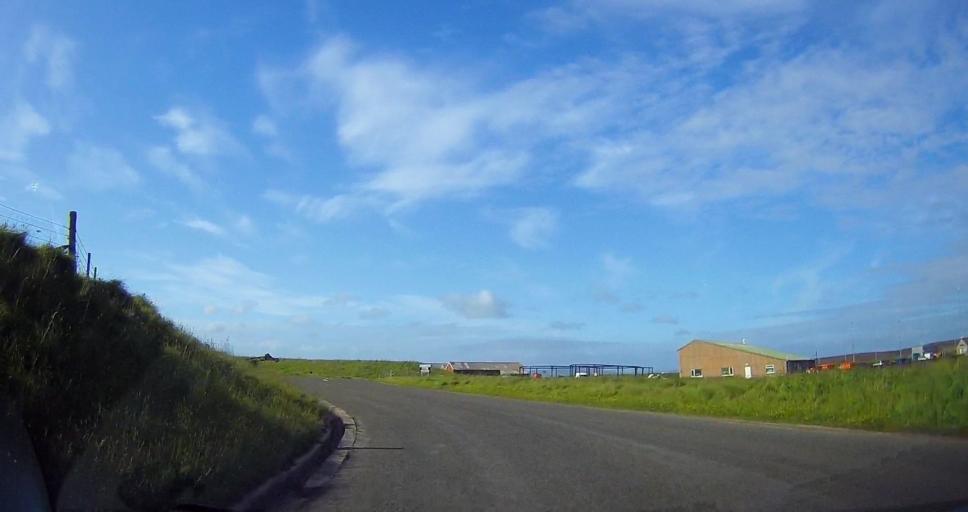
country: GB
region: Scotland
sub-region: Orkney Islands
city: Stromness
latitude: 58.8324
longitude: -3.1950
